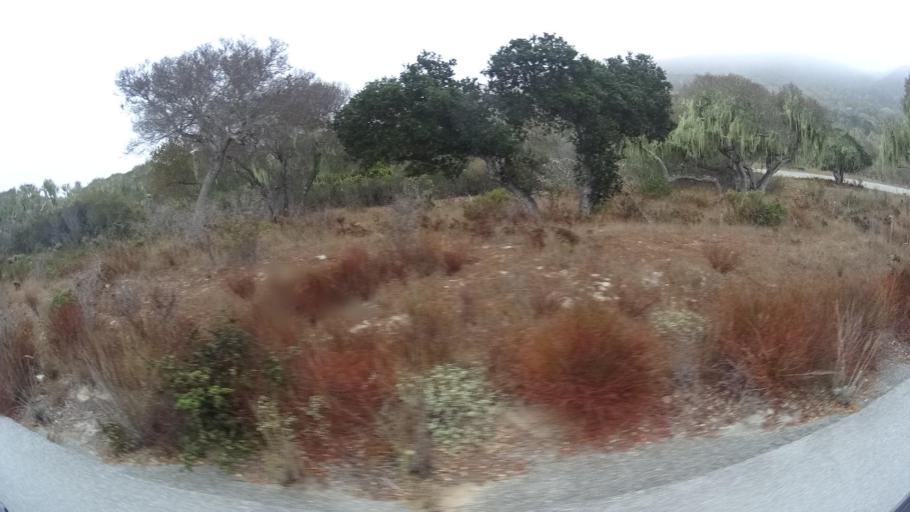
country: US
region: California
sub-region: Monterey County
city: Marina
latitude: 36.6253
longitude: -121.7415
